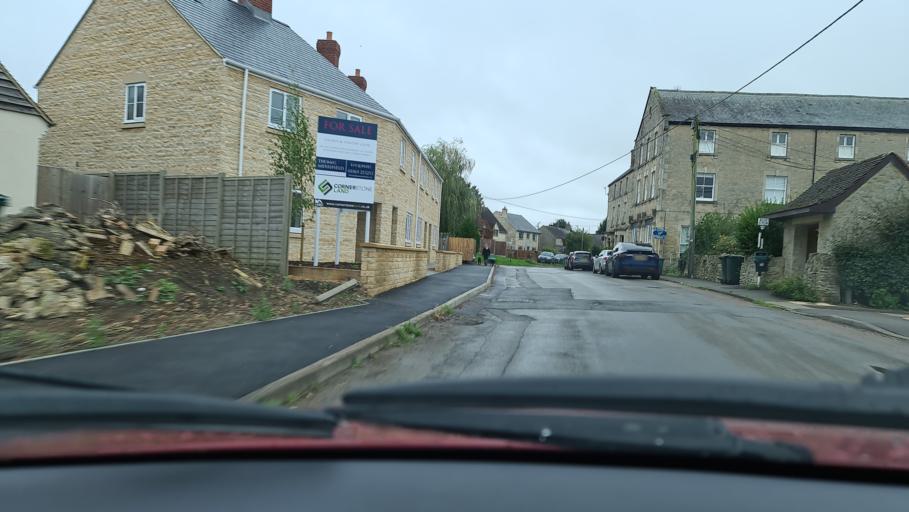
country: GB
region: England
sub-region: Oxfordshire
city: Somerton
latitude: 51.9604
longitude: -1.2330
